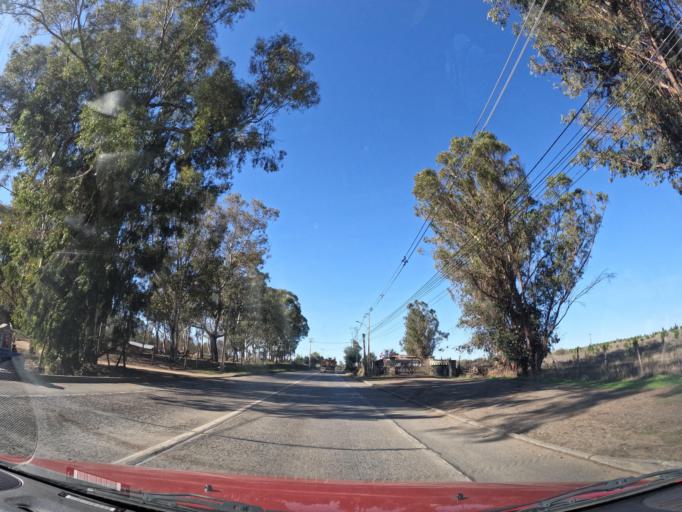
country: CL
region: Maule
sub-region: Provincia de Cauquenes
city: Cauquenes
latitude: -35.9575
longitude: -72.2794
